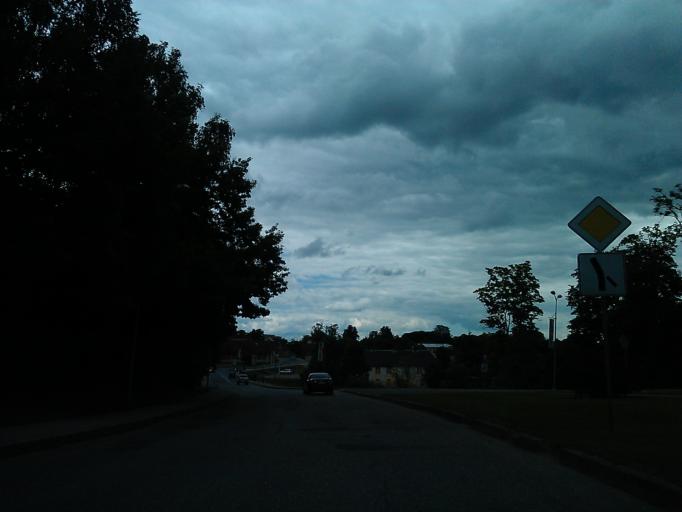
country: LV
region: Dobeles Rajons
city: Dobele
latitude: 56.6236
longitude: 23.2715
